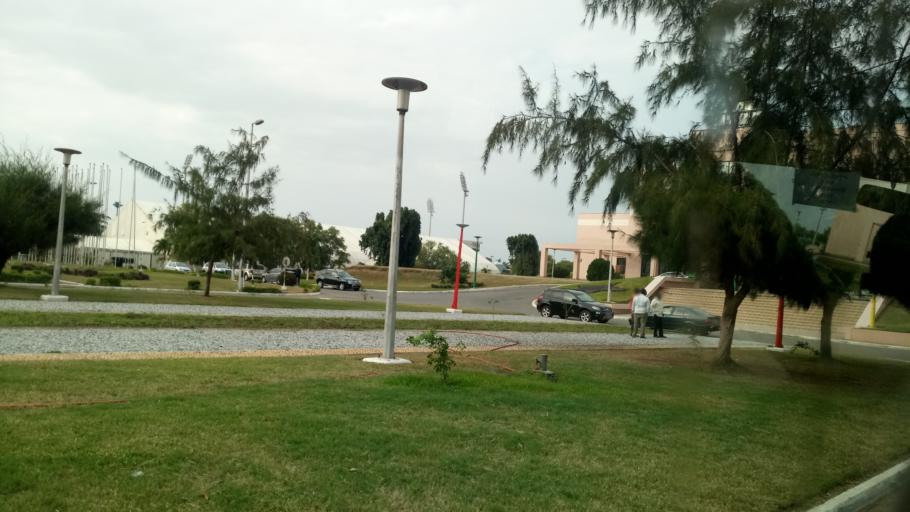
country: GH
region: Greater Accra
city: Accra
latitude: 5.5553
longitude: -0.1930
